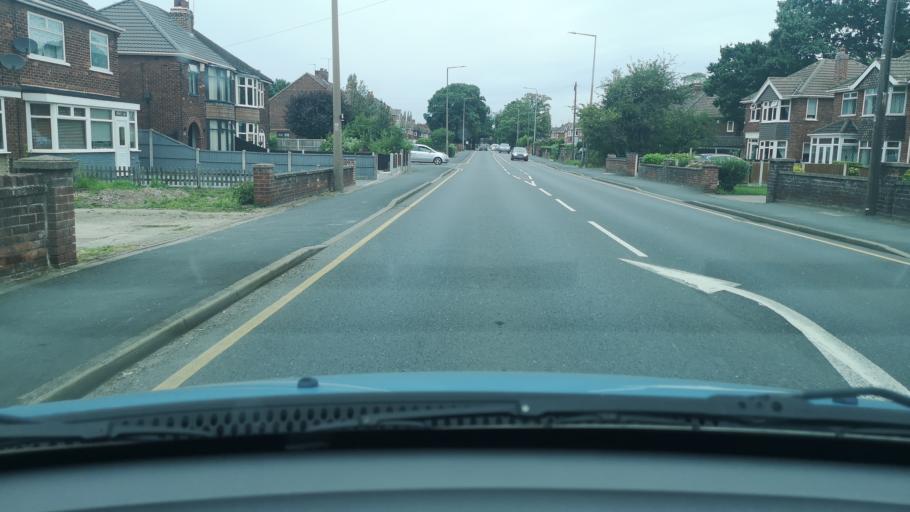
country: GB
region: England
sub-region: North Lincolnshire
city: Scunthorpe
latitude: 53.5855
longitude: -0.6843
